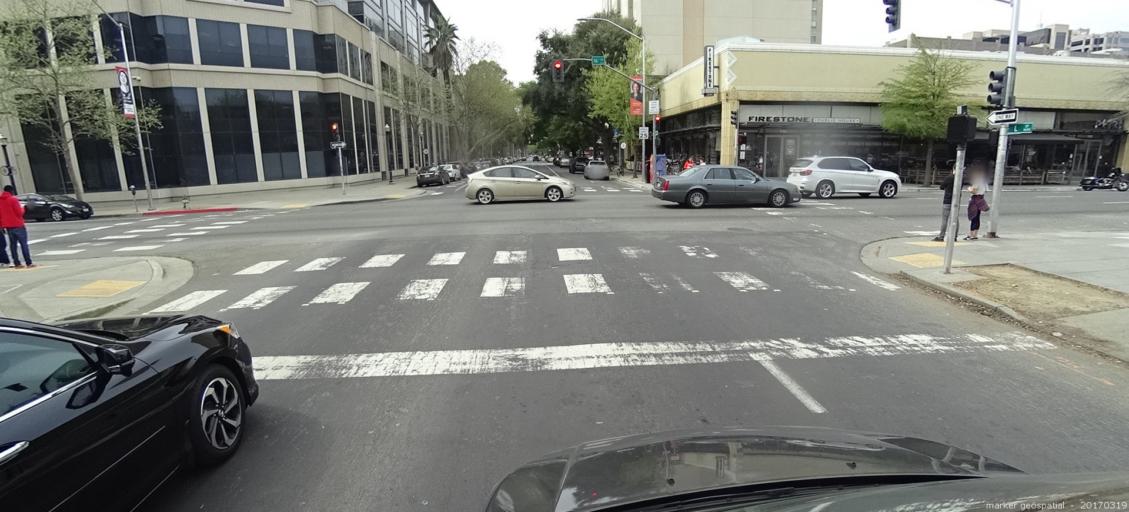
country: US
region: California
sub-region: Sacramento County
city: Sacramento
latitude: 38.5758
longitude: -121.4860
